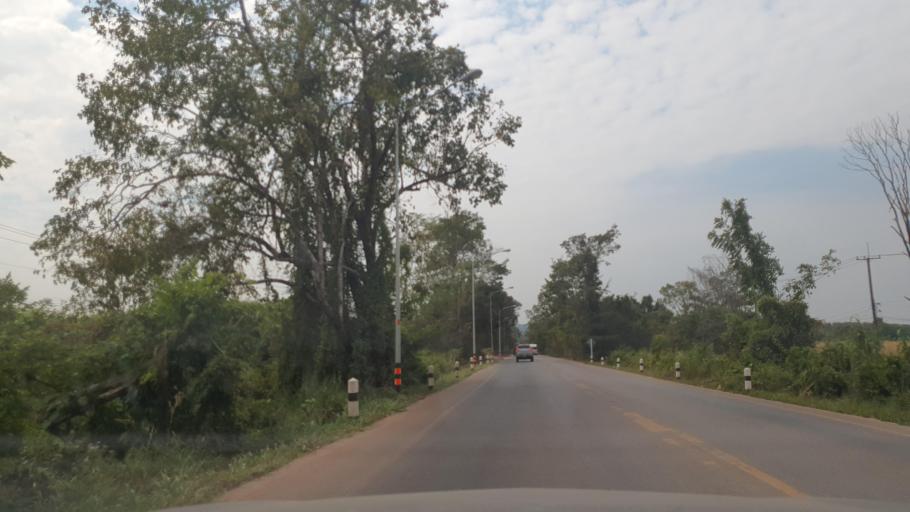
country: TH
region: Changwat Bueng Kan
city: Bung Khla
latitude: 18.2736
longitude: 103.8466
